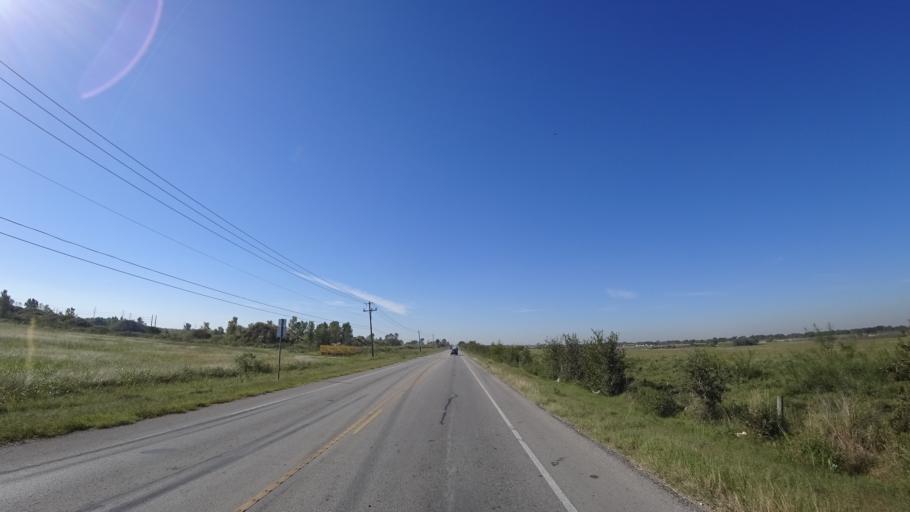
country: US
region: Texas
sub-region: Travis County
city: Hornsby Bend
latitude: 30.2539
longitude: -97.6138
